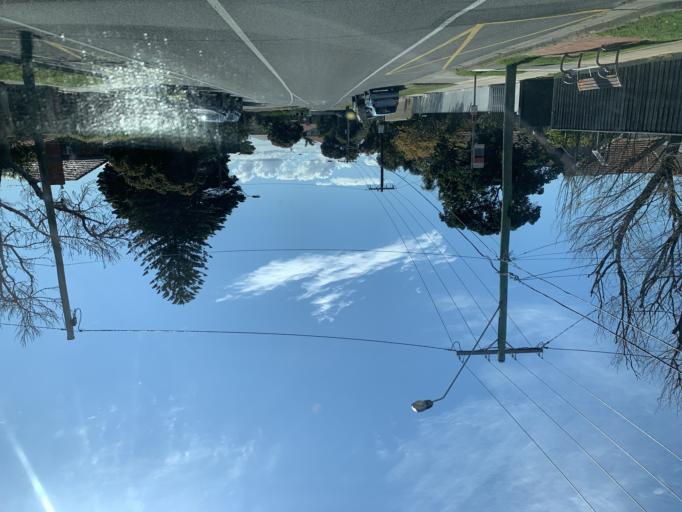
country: AU
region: Victoria
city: Hampton
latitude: -37.9582
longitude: 145.0123
